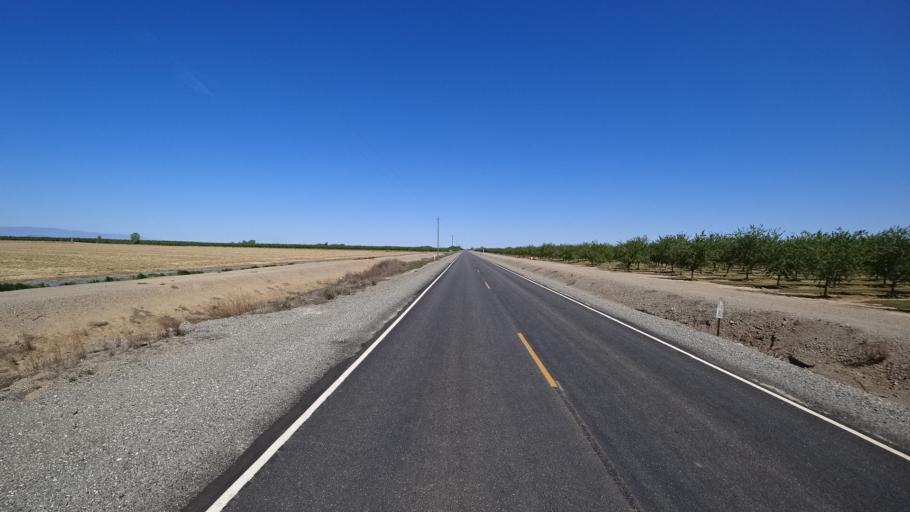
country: US
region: California
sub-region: Glenn County
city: Orland
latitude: 39.6574
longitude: -122.1408
